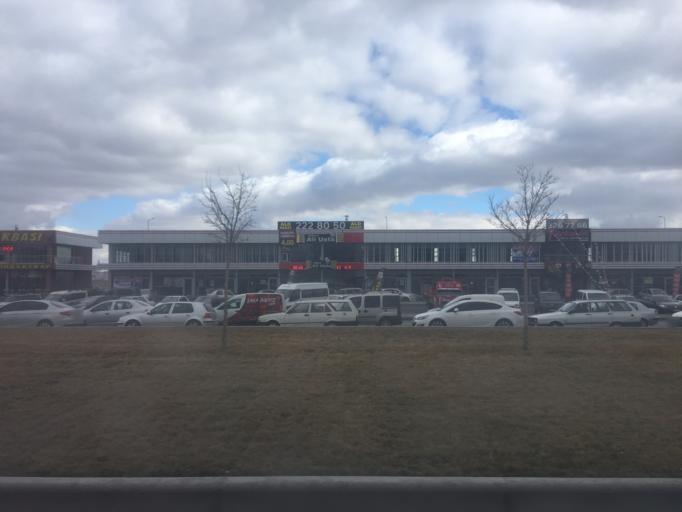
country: TR
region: Kayseri
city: Melikgazi
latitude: 38.7692
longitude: 35.4125
